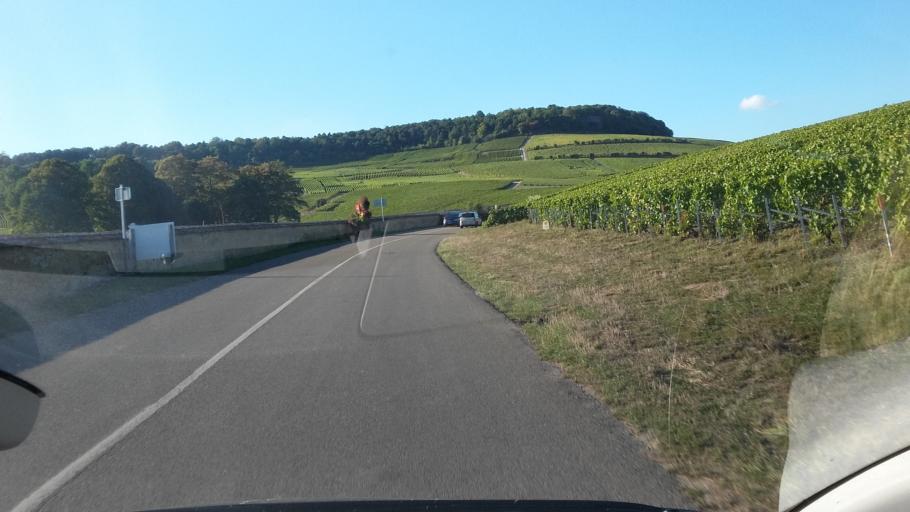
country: FR
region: Champagne-Ardenne
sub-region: Departement de la Marne
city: Avize
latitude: 48.9597
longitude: 4.0121
